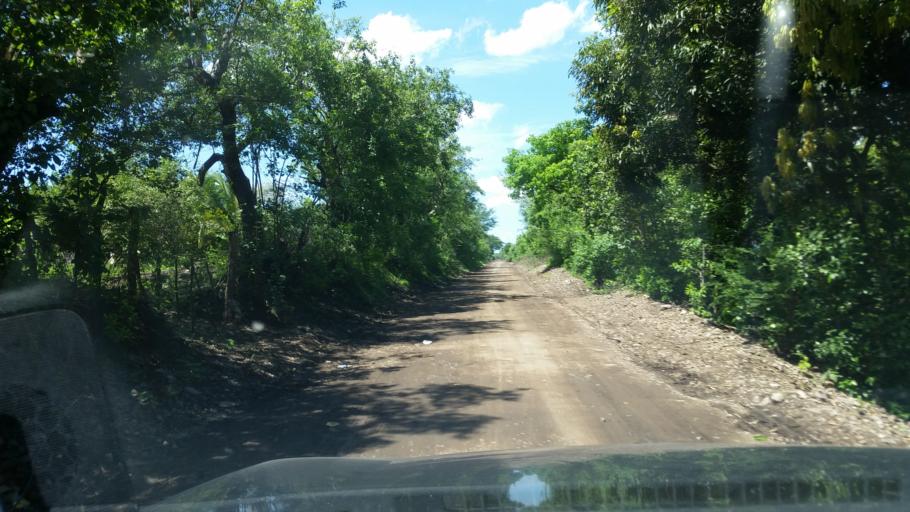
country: NI
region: Chinandega
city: Puerto Morazan
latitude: 12.7595
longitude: -87.1334
